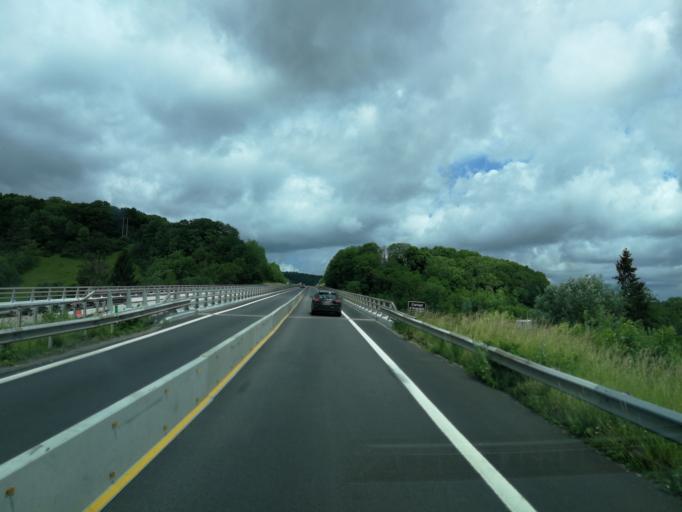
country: FR
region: Haute-Normandie
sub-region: Departement de l'Eure
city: Acquigny
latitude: 49.1616
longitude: 1.1792
